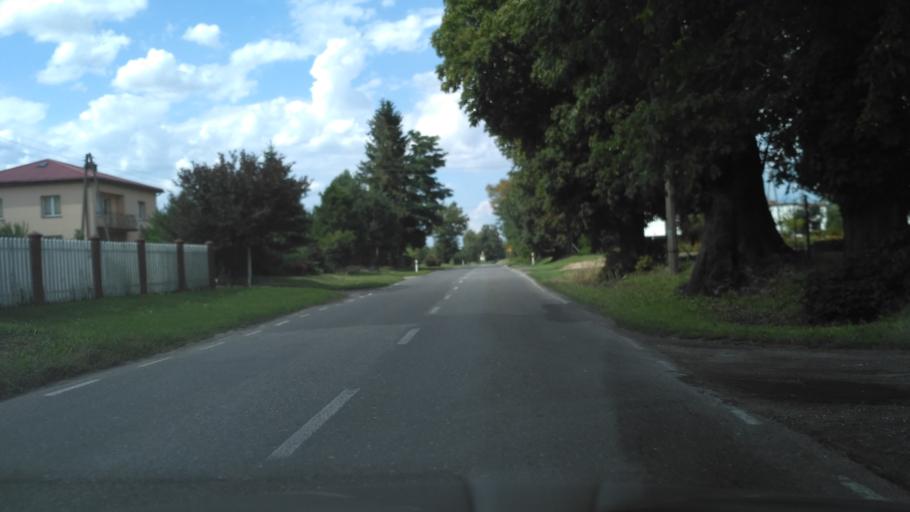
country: PL
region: Lublin Voivodeship
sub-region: Powiat leczynski
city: Milejow
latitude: 51.2048
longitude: 22.9345
